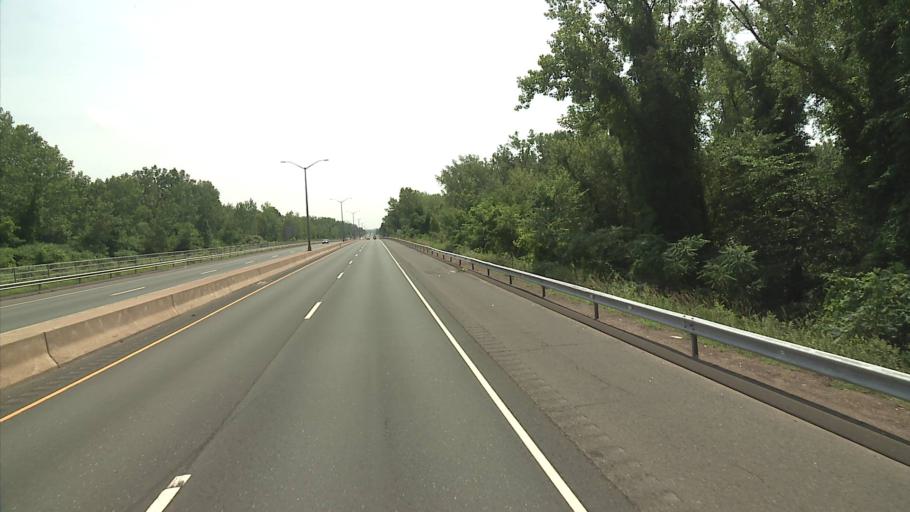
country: US
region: Connecticut
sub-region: Hartford County
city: South Windsor
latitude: 41.8109
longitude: -72.6361
